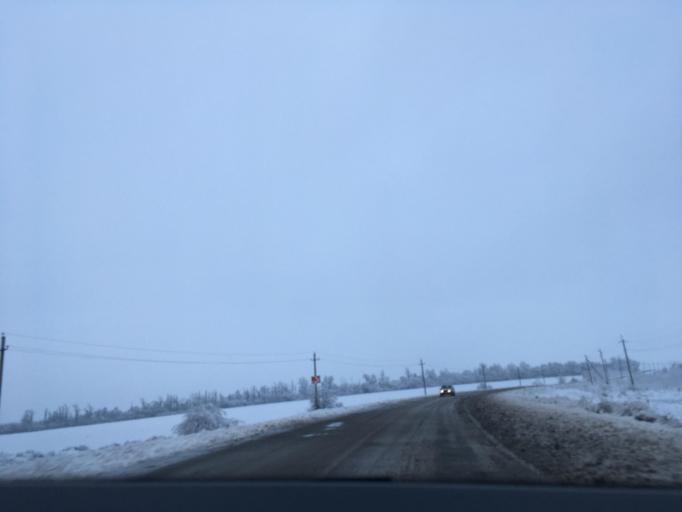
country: RU
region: Voronezj
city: Verkhniy Mamon
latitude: 50.0342
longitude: 40.0603
